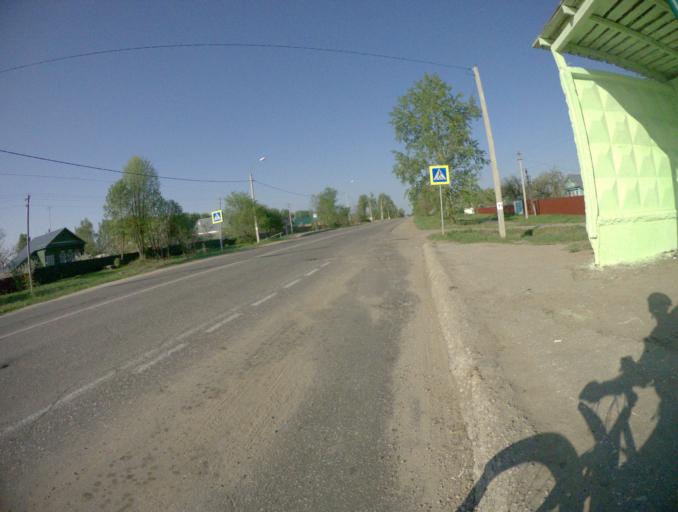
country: RU
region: Vladimir
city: Novovyazniki
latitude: 56.2118
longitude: 42.1719
